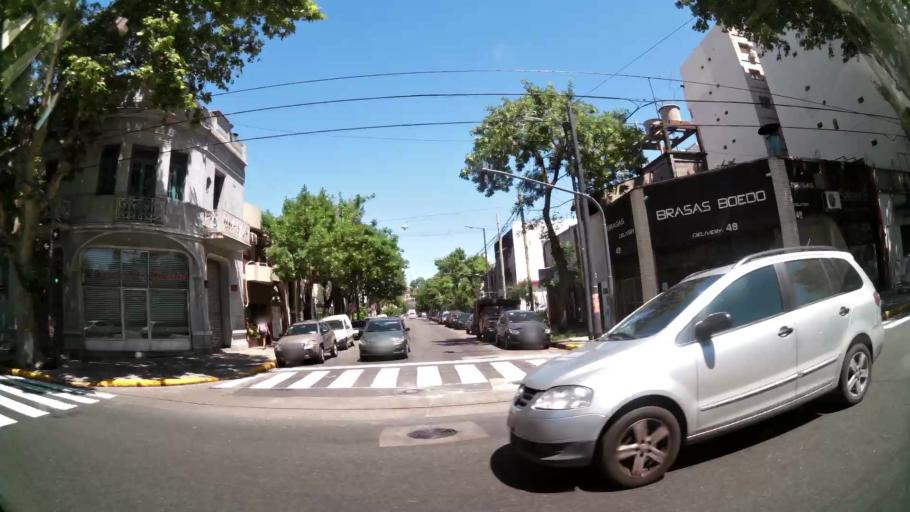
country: AR
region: Buenos Aires F.D.
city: Buenos Aires
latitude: -34.6361
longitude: -58.4163
